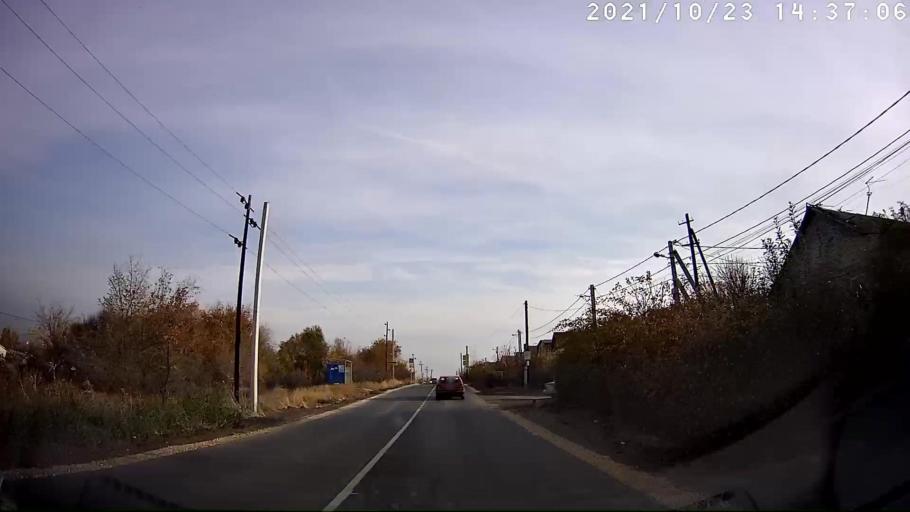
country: RU
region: Volgograd
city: Krasnoslobodsk
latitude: 48.4993
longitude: 44.5465
